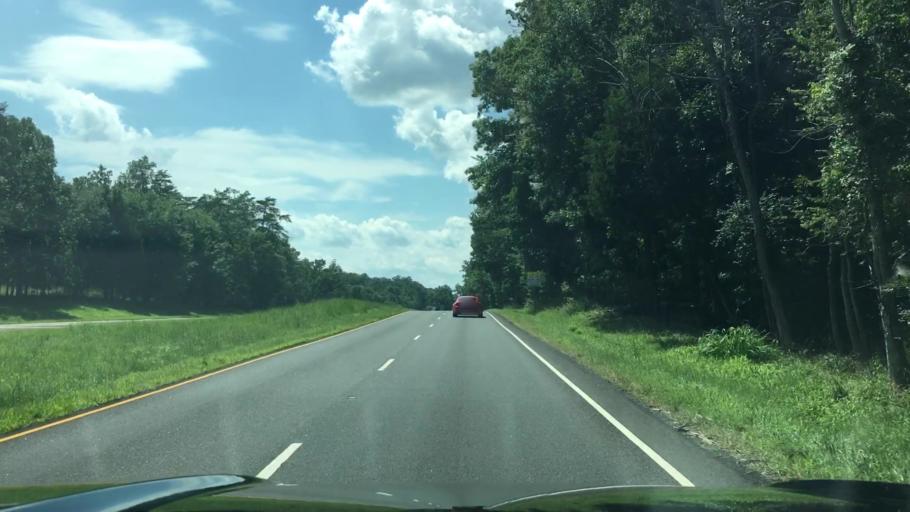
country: US
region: Virginia
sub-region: Prince William County
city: Bull Run
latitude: 38.8096
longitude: -77.5609
